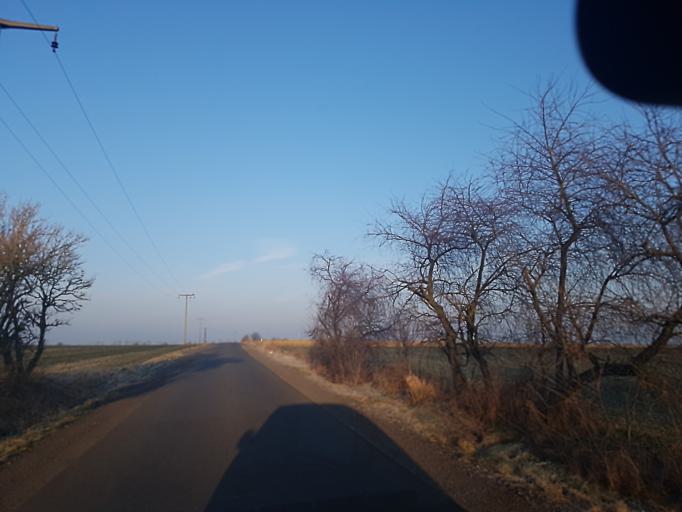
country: DE
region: Brandenburg
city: Niedergorsdorf
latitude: 51.9438
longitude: 13.0065
